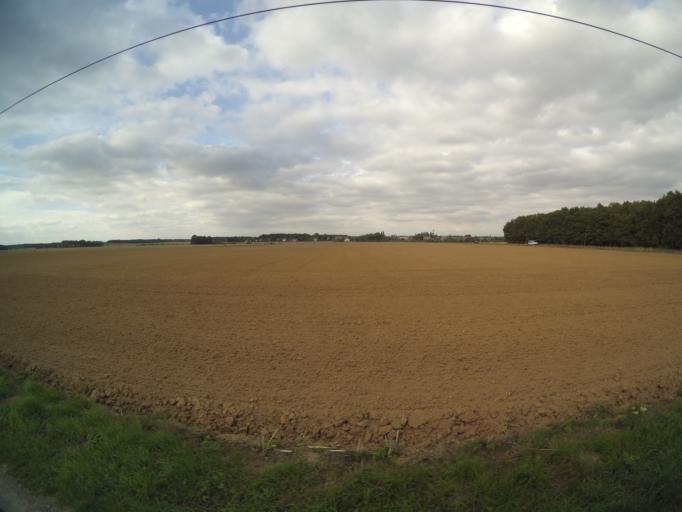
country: FR
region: Centre
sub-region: Departement d'Indre-et-Loire
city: Nazelles-Negron
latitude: 47.4797
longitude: 0.9500
